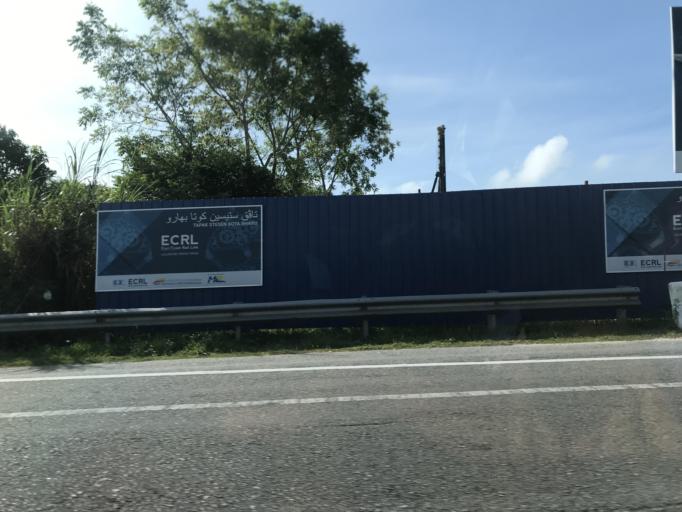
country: MY
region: Kelantan
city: Kampong Kadok
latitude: 6.0553
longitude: 102.2271
